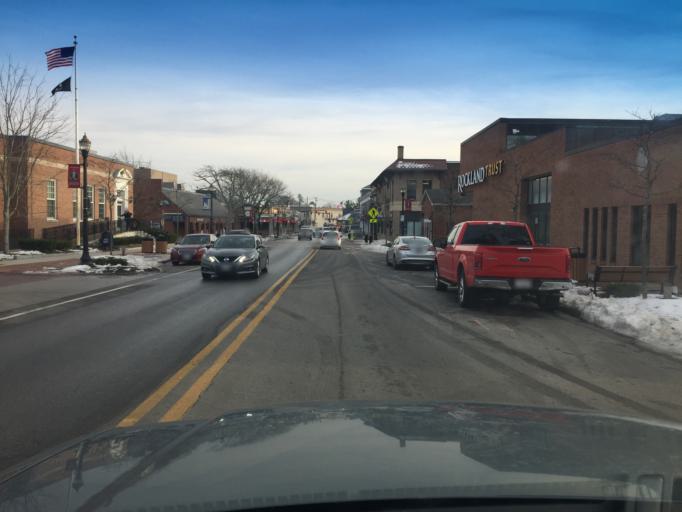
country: US
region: Massachusetts
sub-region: Norfolk County
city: Franklin
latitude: 42.0842
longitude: -71.3985
